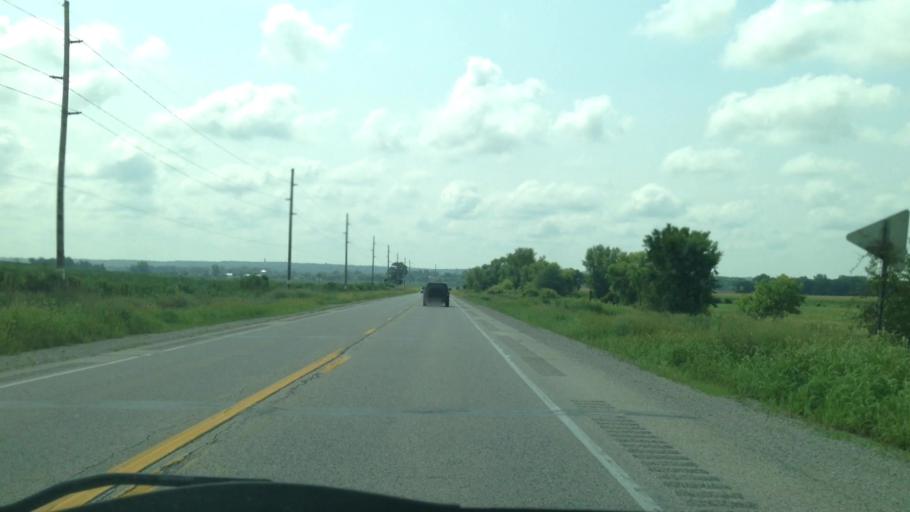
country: US
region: Iowa
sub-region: Benton County
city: Walford
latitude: 41.8209
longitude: -91.8728
